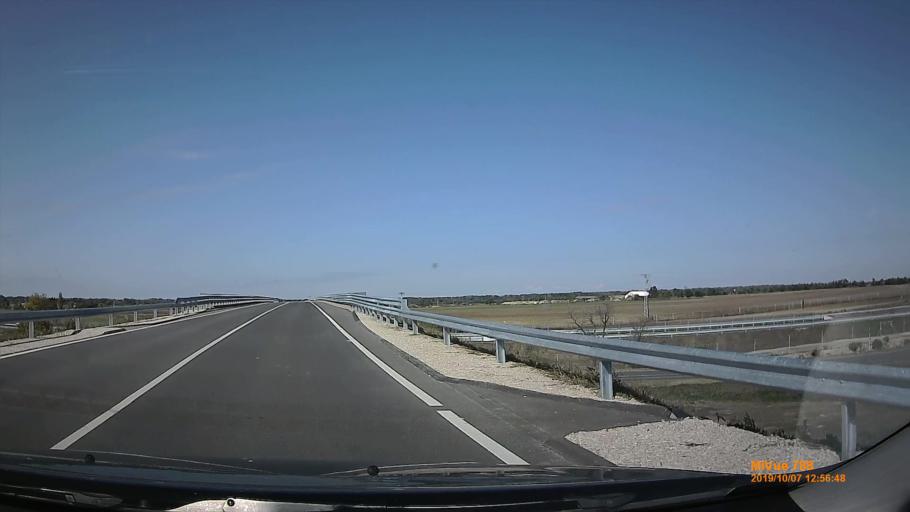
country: HU
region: Jasz-Nagykun-Szolnok
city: Cserkeszolo
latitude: 46.8789
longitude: 20.1427
